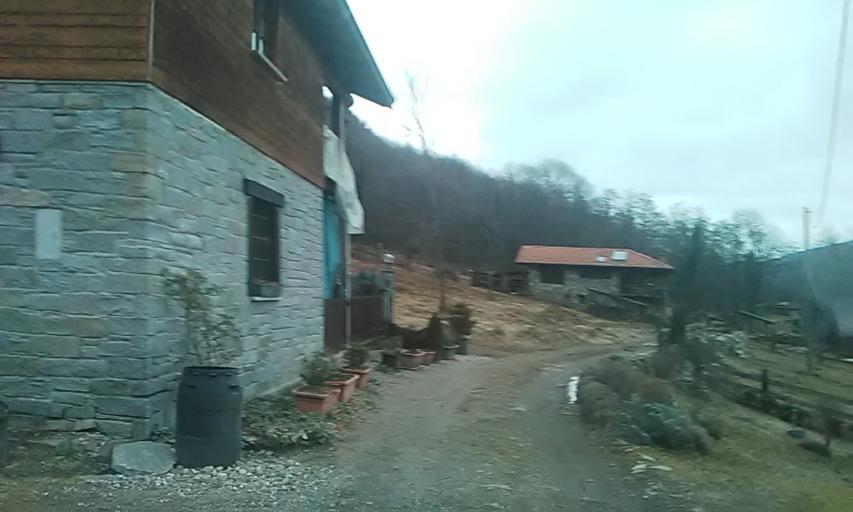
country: IT
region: Piedmont
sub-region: Provincia di Vercelli
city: Quarona
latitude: 45.7831
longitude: 8.2404
